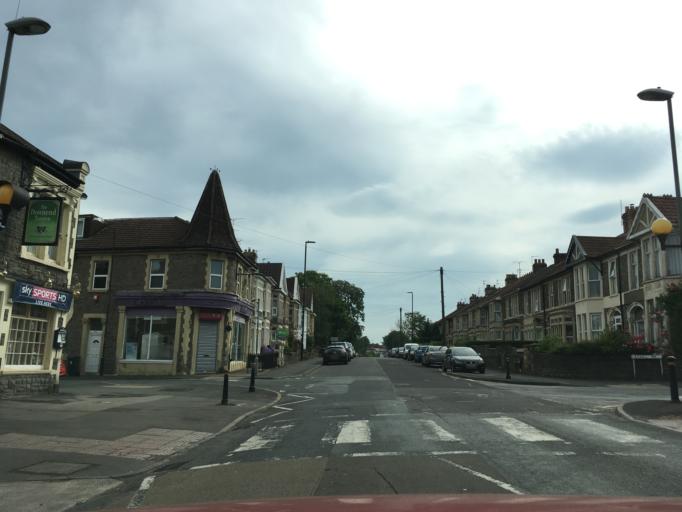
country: GB
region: England
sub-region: South Gloucestershire
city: Mangotsfield
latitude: 51.4844
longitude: -2.5170
